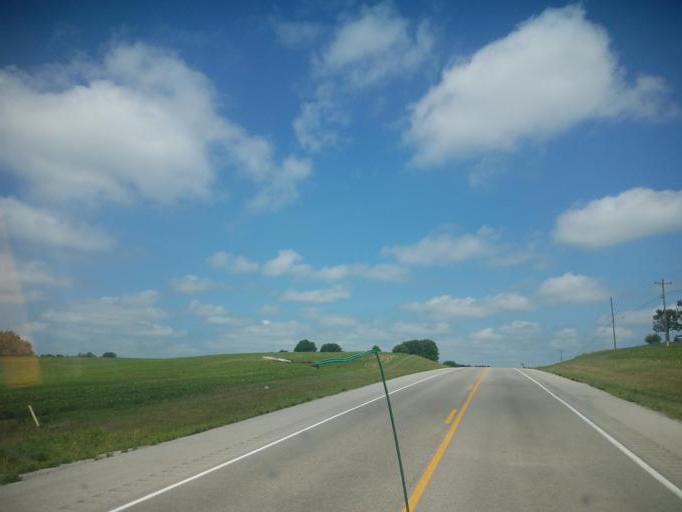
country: US
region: Kentucky
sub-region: Barren County
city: Glasgow
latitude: 36.9288
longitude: -85.8100
